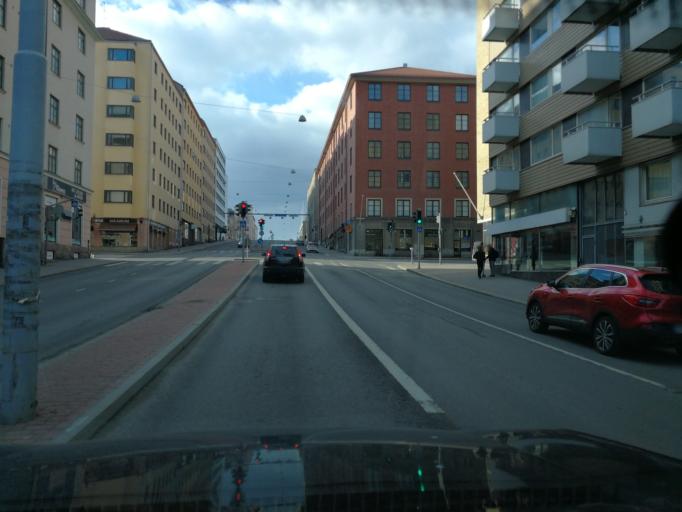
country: FI
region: Varsinais-Suomi
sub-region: Turku
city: Turku
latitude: 60.4538
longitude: 22.2726
